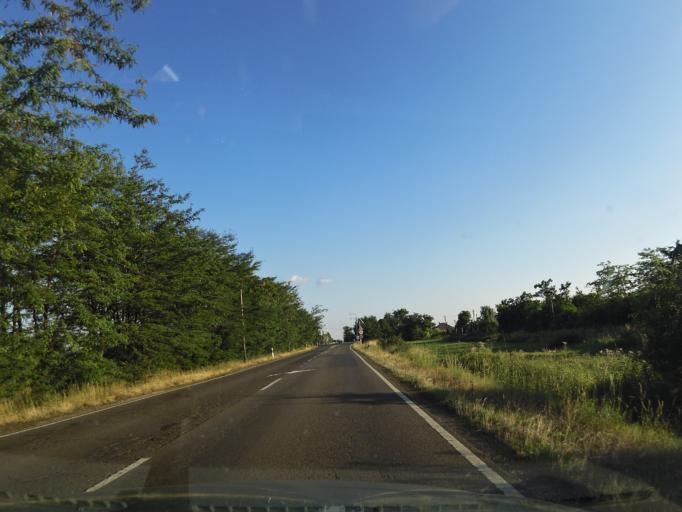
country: HU
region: Jasz-Nagykun-Szolnok
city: Tiszafoldvar
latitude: 46.9489
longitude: 20.2709
